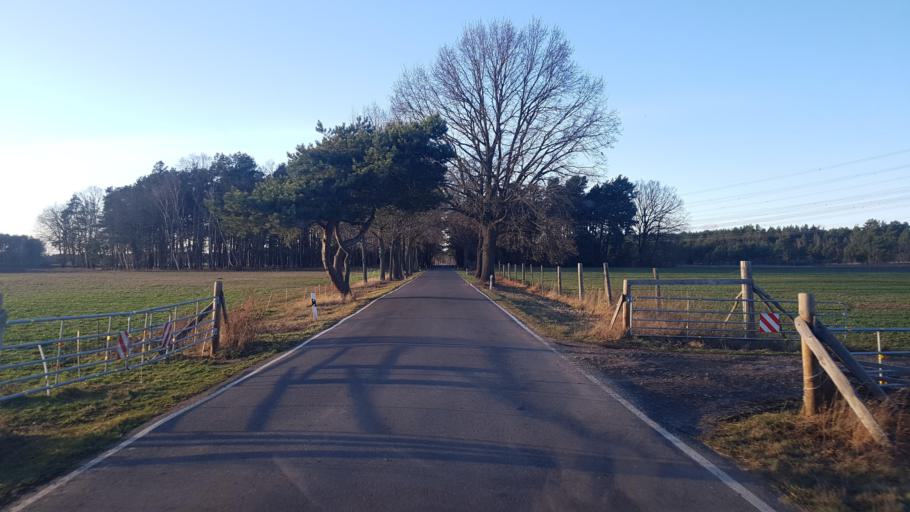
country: DE
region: Brandenburg
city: Drachhausen
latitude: 51.8719
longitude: 14.3327
